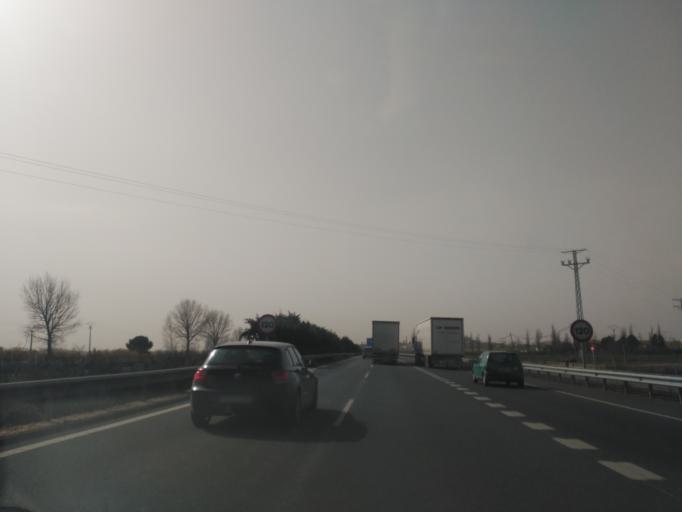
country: ES
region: Castille and Leon
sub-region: Provincia de Valladolid
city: Cabezon
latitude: 41.7414
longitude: -4.6636
